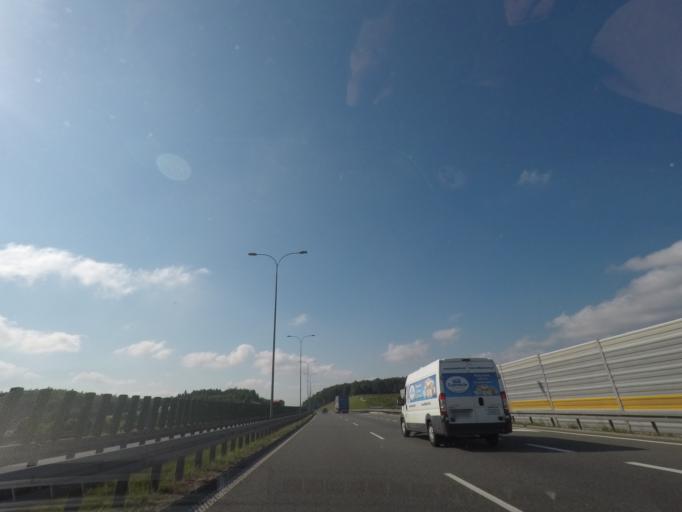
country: PL
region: Pomeranian Voivodeship
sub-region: Powiat tczewski
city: Pelplin
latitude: 53.9288
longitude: 18.6408
